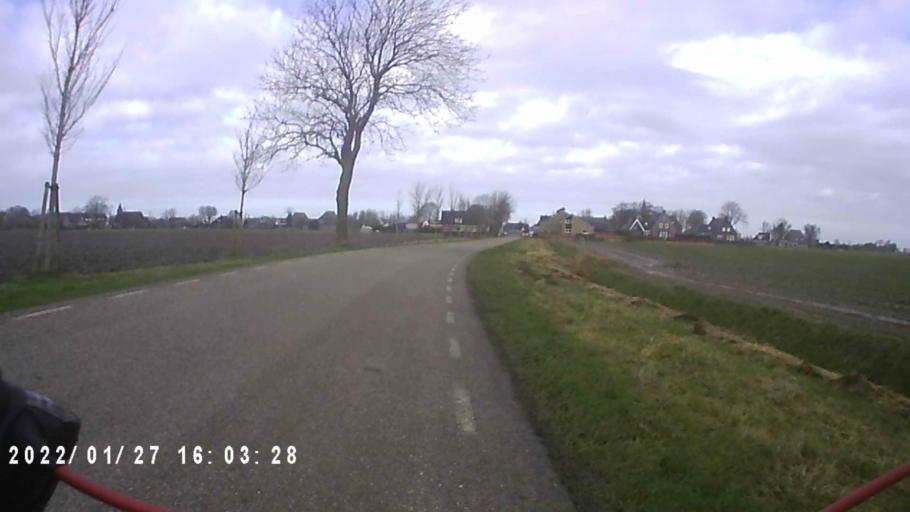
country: NL
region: Friesland
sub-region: Gemeente Dongeradeel
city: Anjum
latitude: 53.3777
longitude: 6.0889
